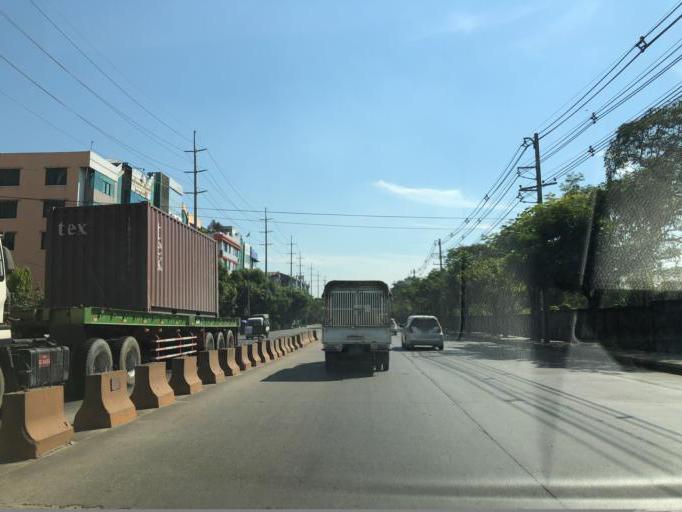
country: MM
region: Yangon
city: Yangon
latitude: 16.8282
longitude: 96.1223
